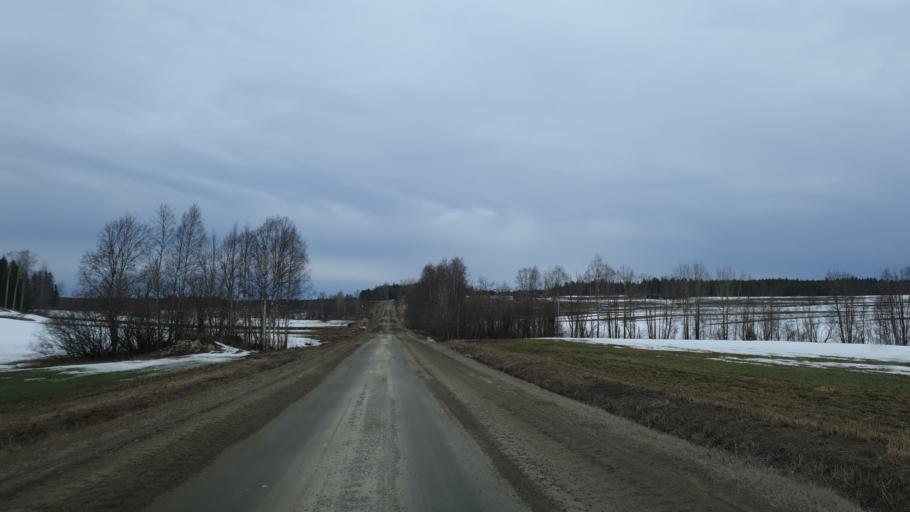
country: SE
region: Vaesterbotten
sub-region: Skelleftea Kommun
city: Burea
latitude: 64.3365
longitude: 21.1303
